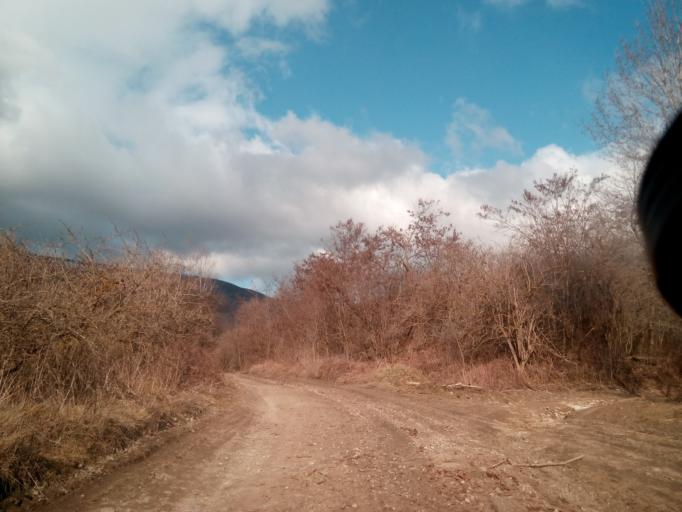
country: SK
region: Banskobystricky
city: Revuca
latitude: 48.7261
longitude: 20.2428
